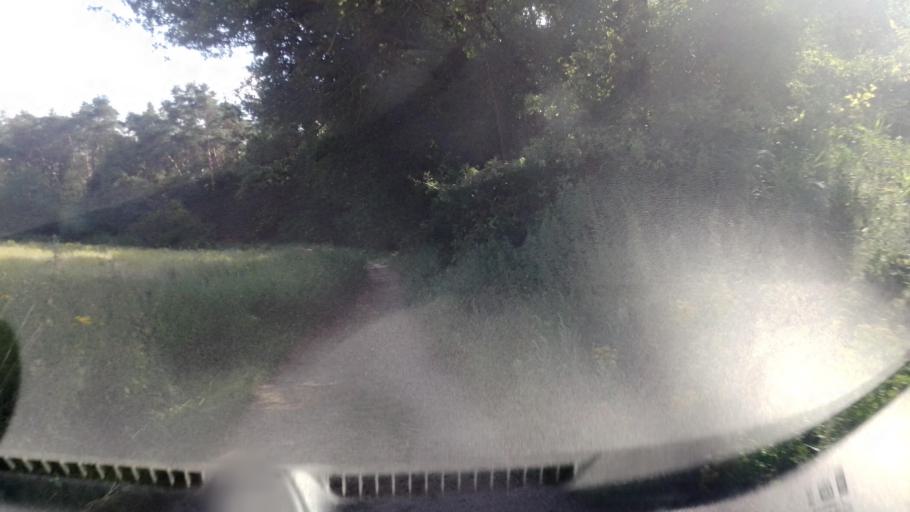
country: NL
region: Limburg
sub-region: Gemeente Venlo
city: Tegelen
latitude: 51.3711
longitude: 6.1038
